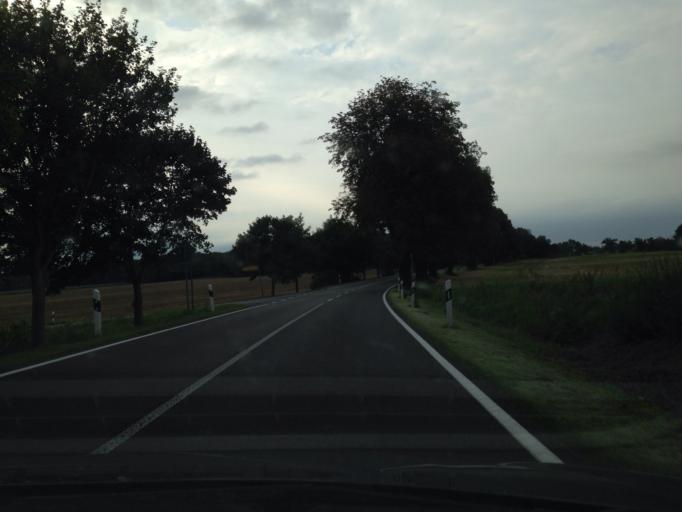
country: DE
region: Mecklenburg-Vorpommern
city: Loitz
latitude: 53.3713
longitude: 13.3618
